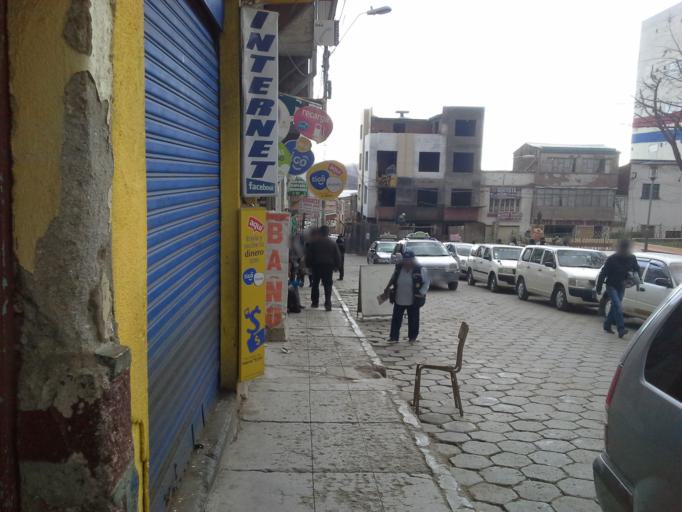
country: BO
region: Potosi
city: Llallagua
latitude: -18.4230
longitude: -66.5857
